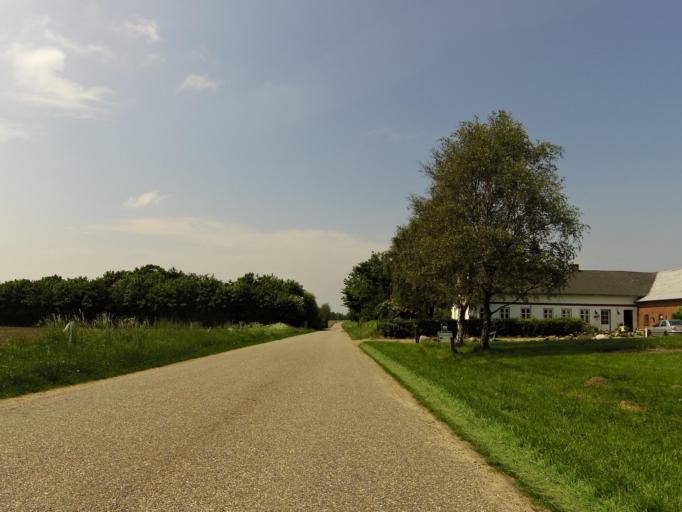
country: DK
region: South Denmark
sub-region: Tonder Kommune
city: Toftlund
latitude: 55.1874
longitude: 9.0355
